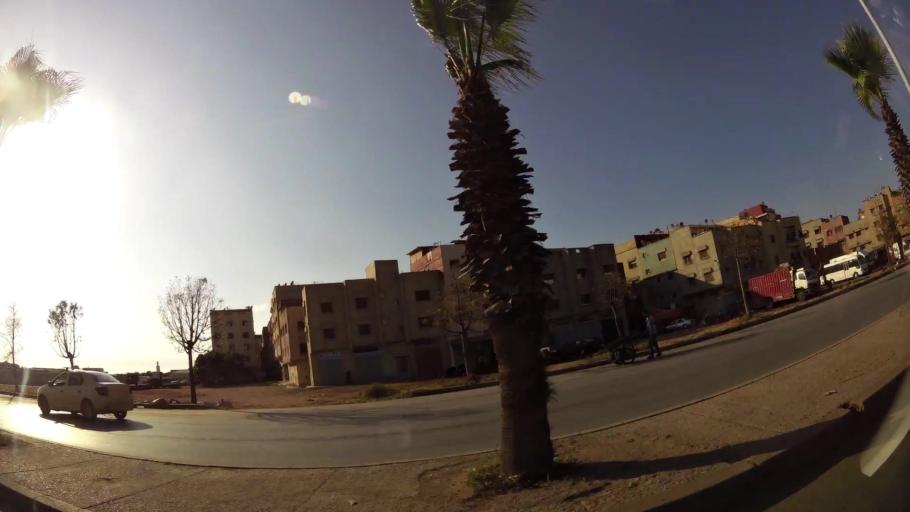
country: MA
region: Rabat-Sale-Zemmour-Zaer
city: Sale
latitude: 34.0573
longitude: -6.7888
